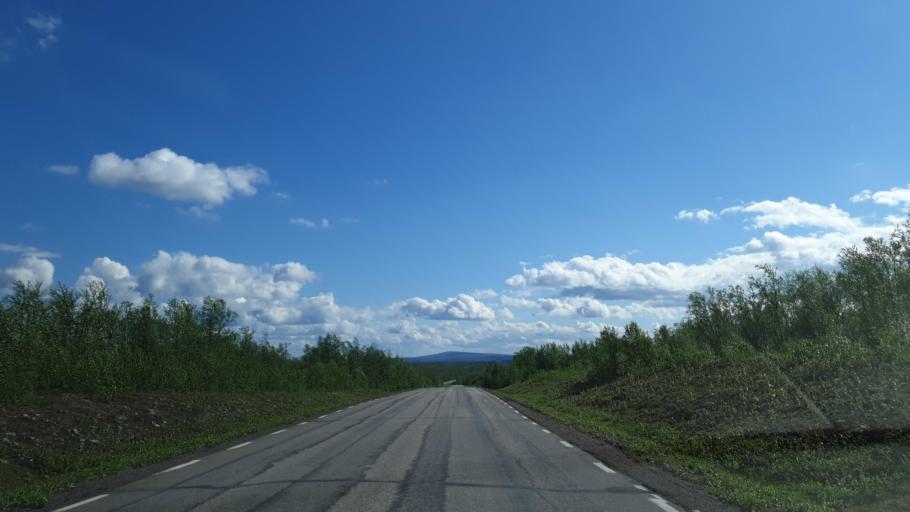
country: SE
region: Norrbotten
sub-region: Kiruna Kommun
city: Kiruna
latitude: 67.7932
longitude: 20.2314
